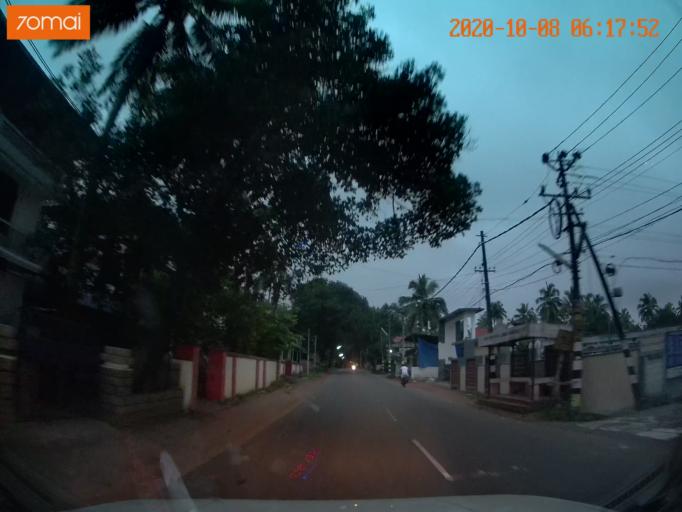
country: IN
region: Kerala
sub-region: Thrissur District
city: Trichur
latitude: 10.5124
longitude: 76.2534
